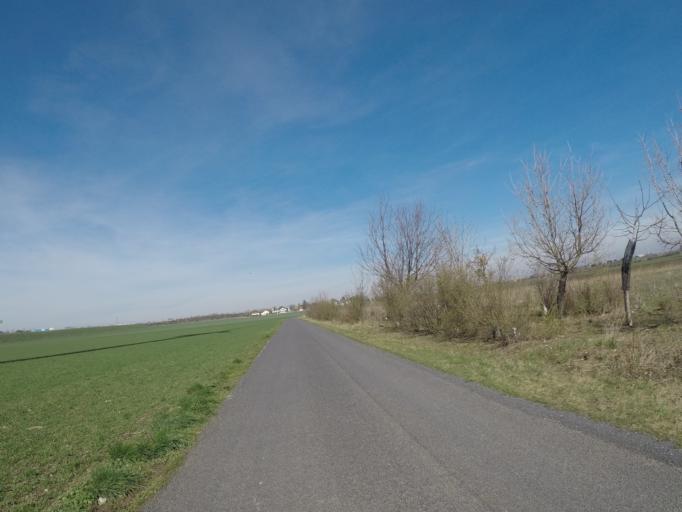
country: AT
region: Lower Austria
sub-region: Politischer Bezirk Modling
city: Vosendorf
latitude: 48.1115
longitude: 16.3256
